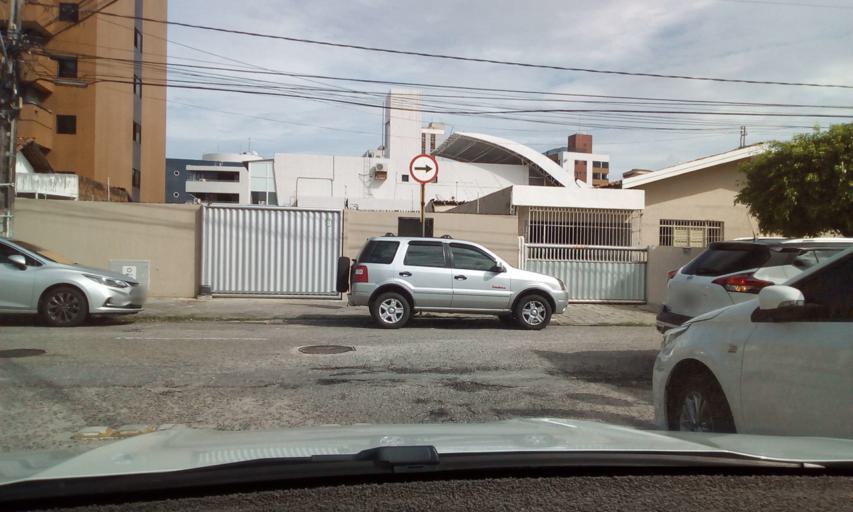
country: BR
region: Paraiba
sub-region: Joao Pessoa
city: Joao Pessoa
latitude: -7.1006
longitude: -34.8333
